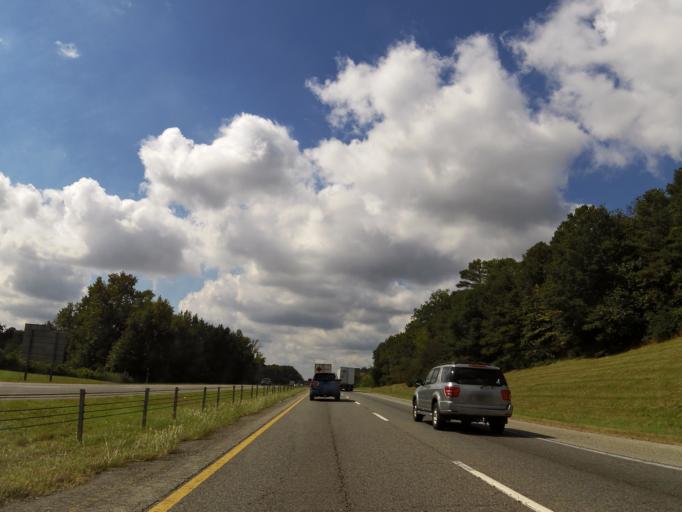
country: US
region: Alabama
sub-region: Jefferson County
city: Bessemer
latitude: 33.3581
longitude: -87.0091
